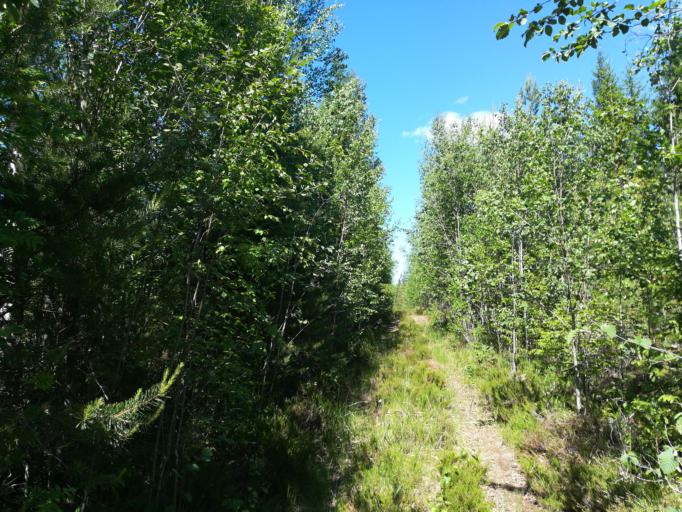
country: FI
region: Southern Savonia
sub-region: Mikkeli
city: Puumala
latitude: 61.6193
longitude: 28.1616
